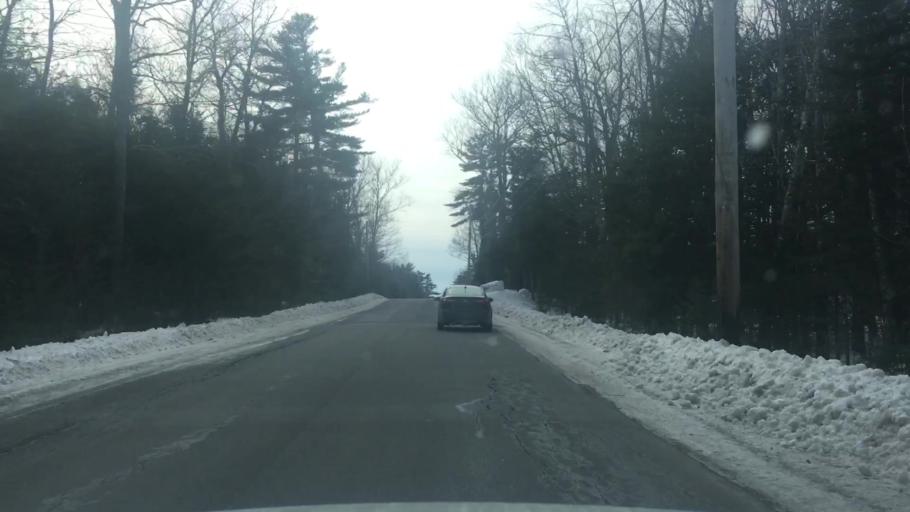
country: US
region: Maine
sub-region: Hancock County
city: Orland
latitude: 44.6054
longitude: -68.7178
